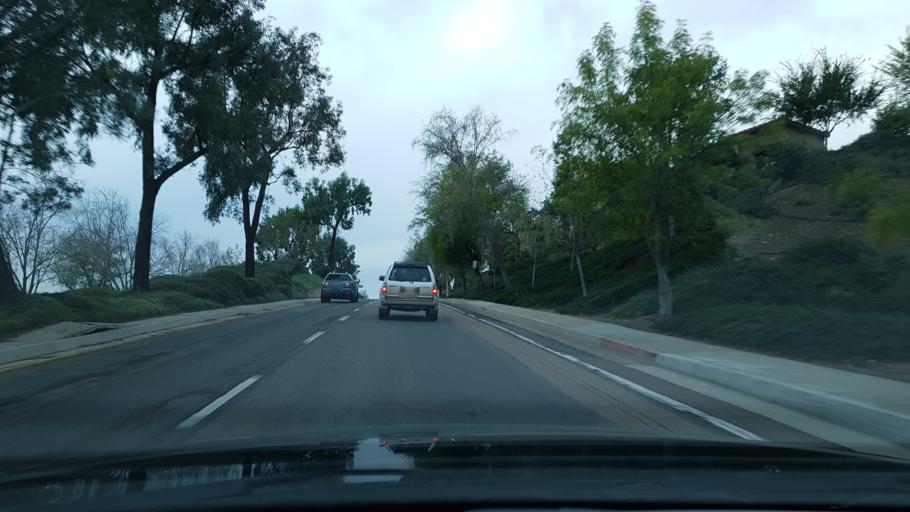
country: US
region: California
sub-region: San Diego County
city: Poway
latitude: 32.9757
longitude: -117.0917
